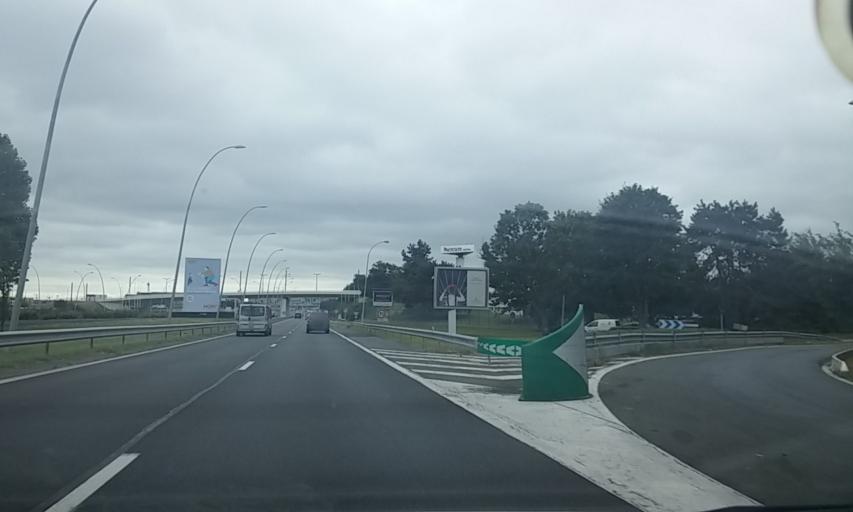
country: FR
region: Ile-de-France
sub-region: Departement du Val-de-Marne
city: Rungis
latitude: 48.7421
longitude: 2.3624
